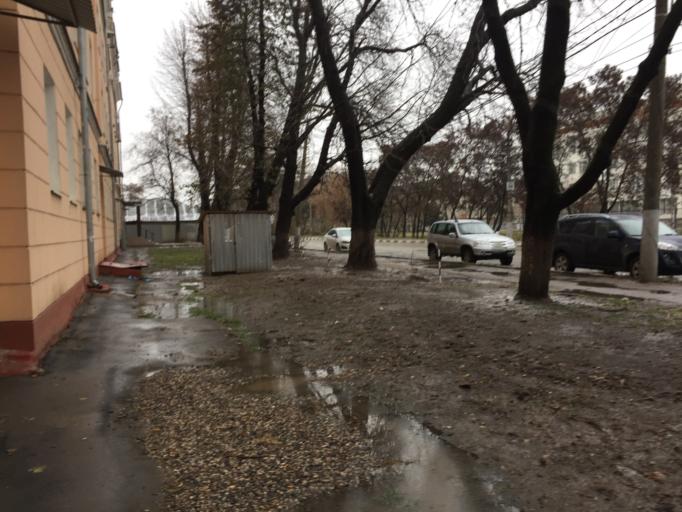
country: RU
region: Tula
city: Tula
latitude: 54.1864
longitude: 37.6238
